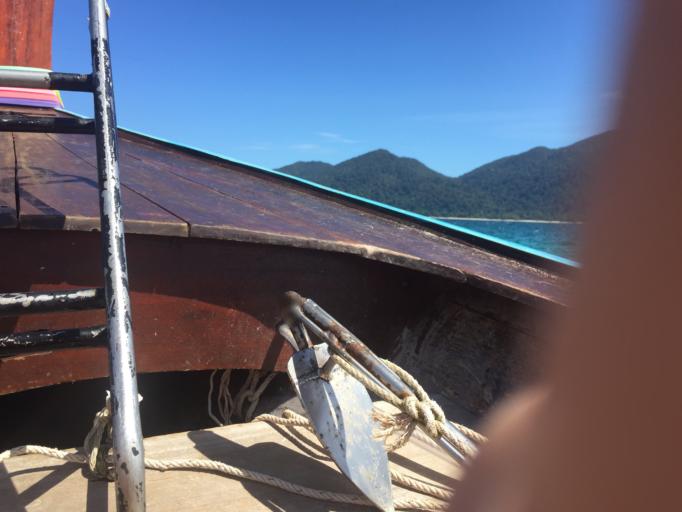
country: MY
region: Kedah
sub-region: Langkawi
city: Kuah
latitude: 6.5137
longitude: 99.2641
